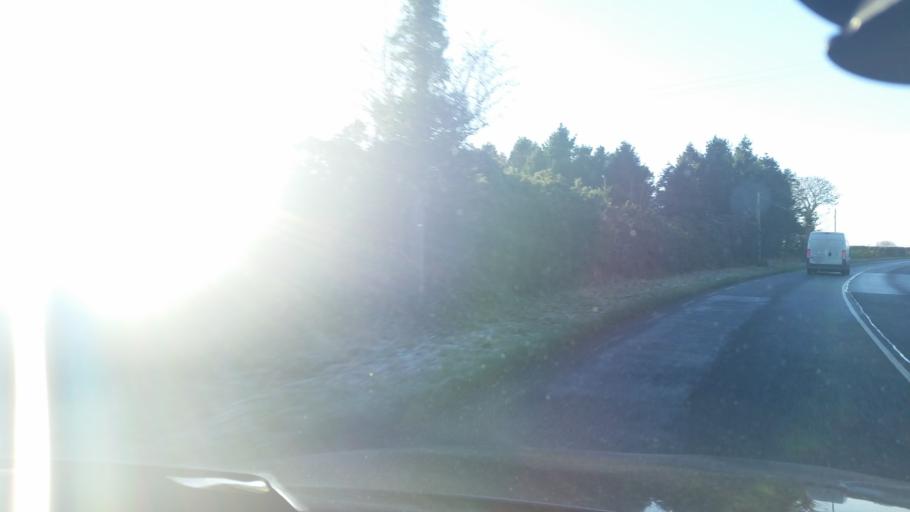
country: IE
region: Leinster
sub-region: Loch Garman
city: Ballinroad
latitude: 52.5411
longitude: -6.3428
